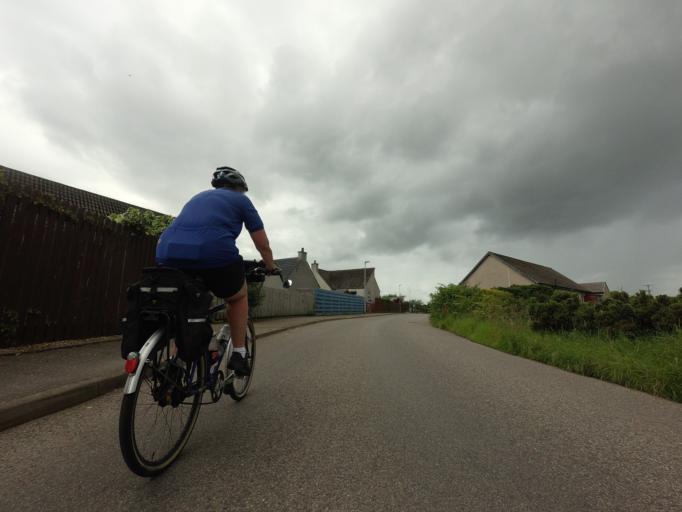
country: GB
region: Scotland
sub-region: Moray
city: Fochabers
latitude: 57.6632
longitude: -3.1141
